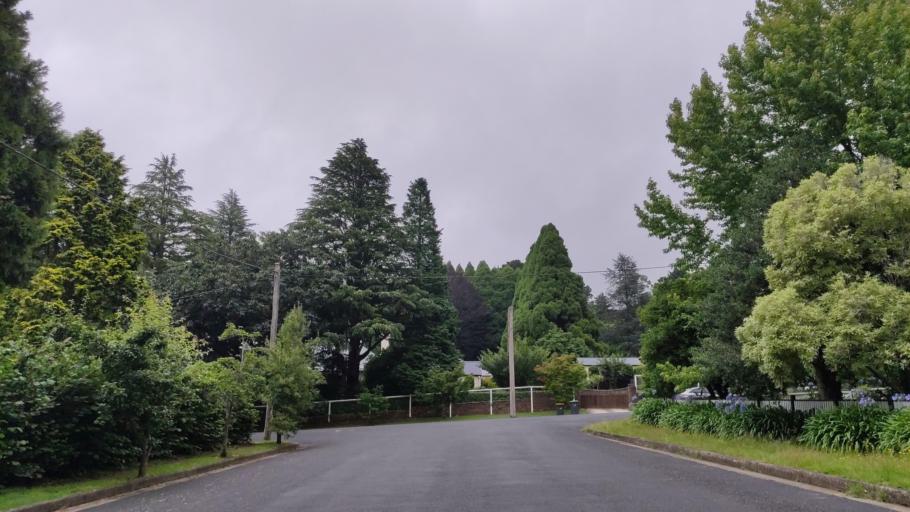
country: AU
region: New South Wales
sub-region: Blue Mountains Municipality
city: Leura
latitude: -33.7189
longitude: 150.3307
